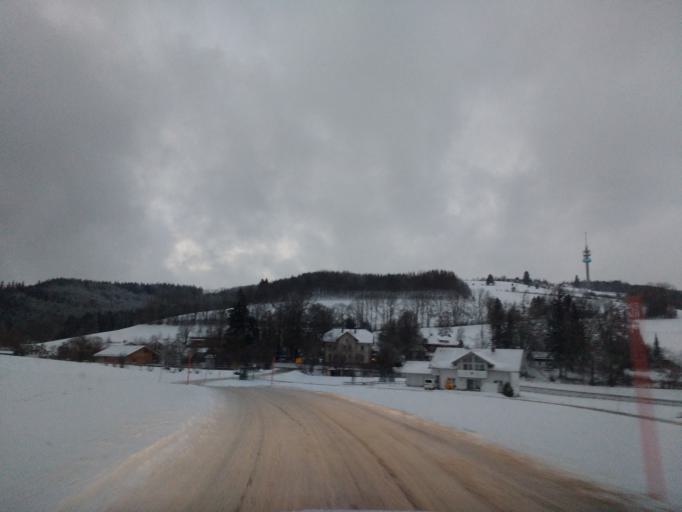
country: DE
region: Bavaria
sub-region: Swabia
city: Buchenberg
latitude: 47.7179
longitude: 10.2175
